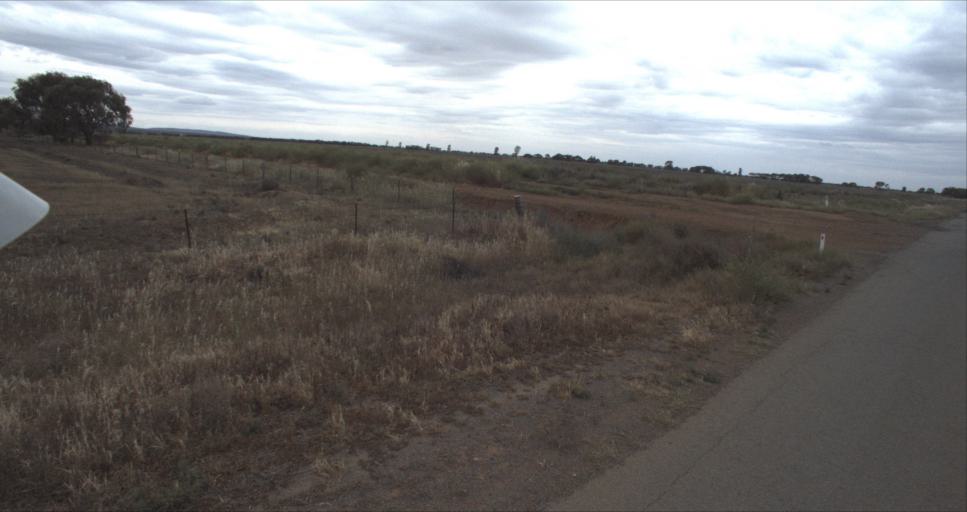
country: AU
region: New South Wales
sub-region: Leeton
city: Leeton
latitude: -34.4229
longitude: 146.3382
